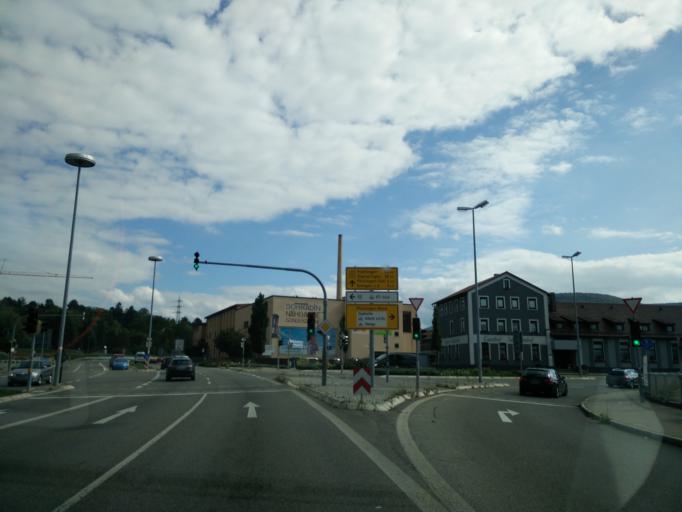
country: DE
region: Baden-Wuerttemberg
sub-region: Tuebingen Region
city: Pfullingen
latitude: 48.4824
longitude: 9.2295
